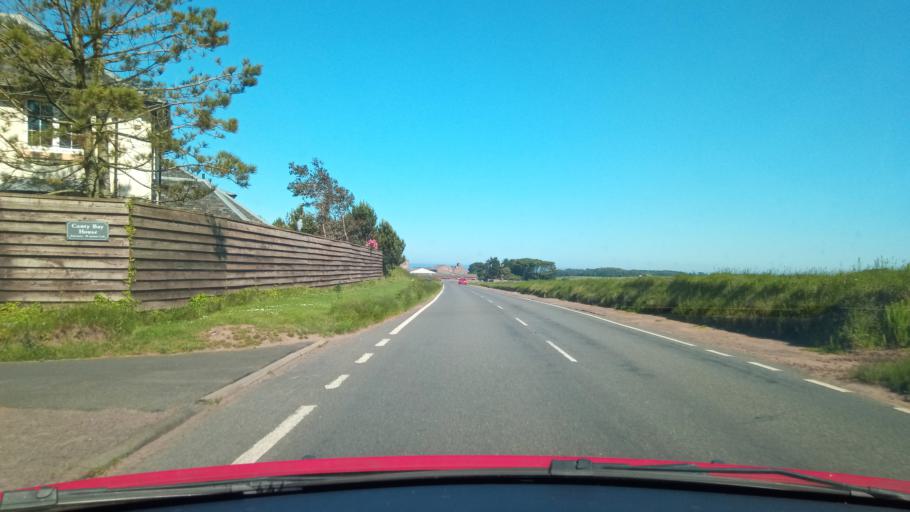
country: GB
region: Scotland
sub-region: East Lothian
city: North Berwick
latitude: 56.0566
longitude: -2.6653
